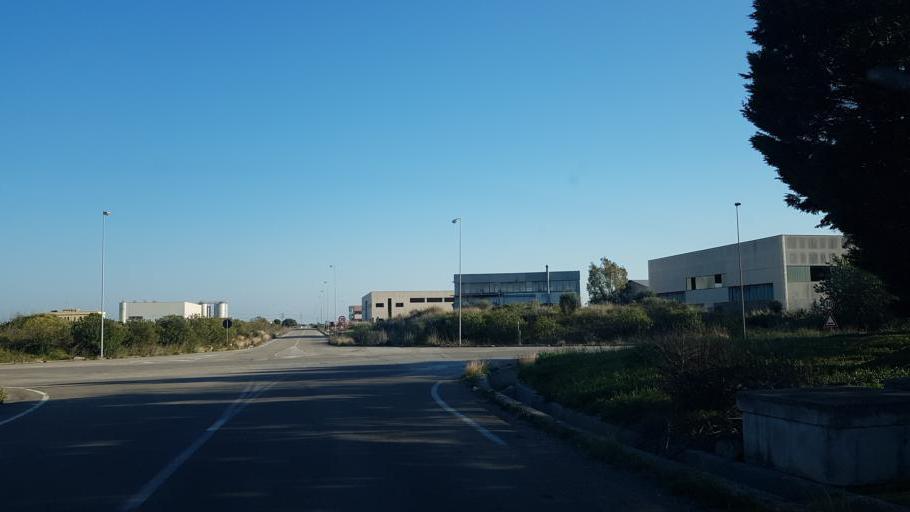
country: IT
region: Apulia
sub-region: Provincia di Brindisi
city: La Rosa
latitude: 40.6261
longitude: 17.9697
